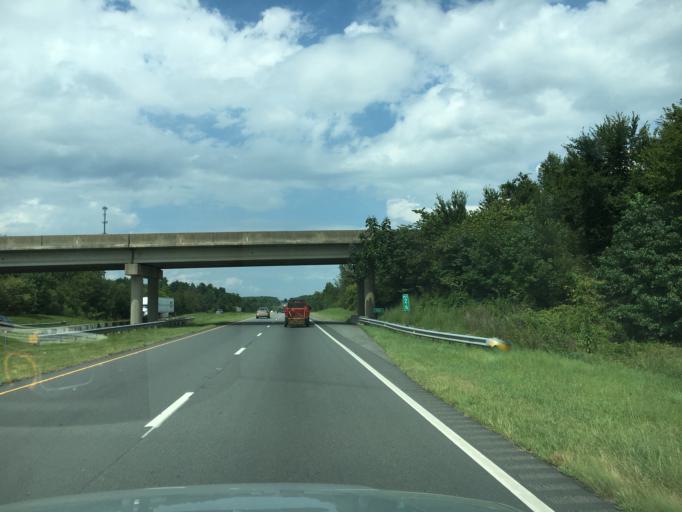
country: US
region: North Carolina
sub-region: Lincoln County
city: Lincolnton
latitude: 35.5045
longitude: -81.2241
